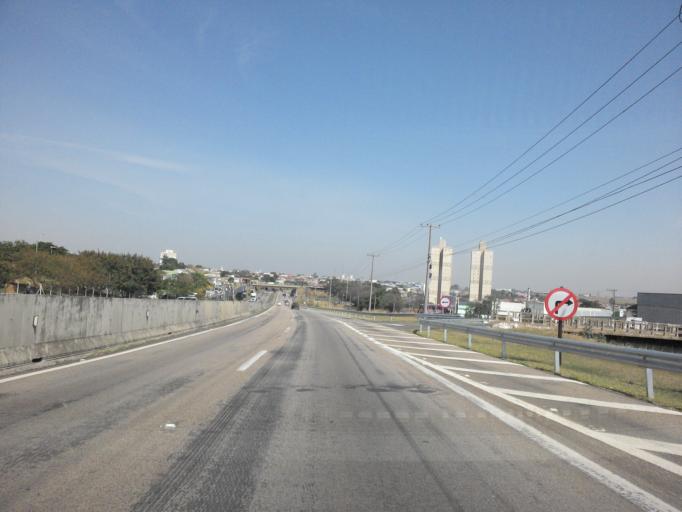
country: BR
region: Sao Paulo
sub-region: Hortolandia
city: Hortolandia
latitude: -22.8869
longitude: -47.1608
